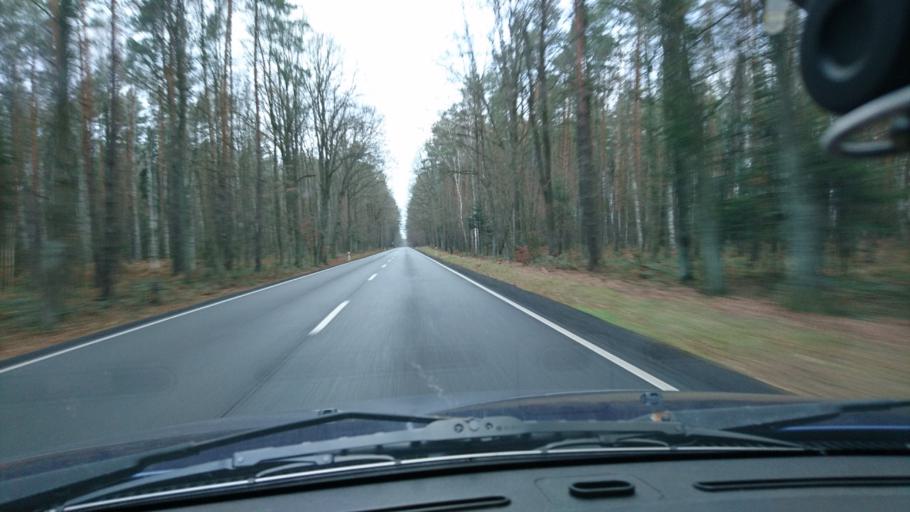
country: PL
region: Opole Voivodeship
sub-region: Powiat oleski
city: Olesno
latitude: 50.9239
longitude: 18.3376
